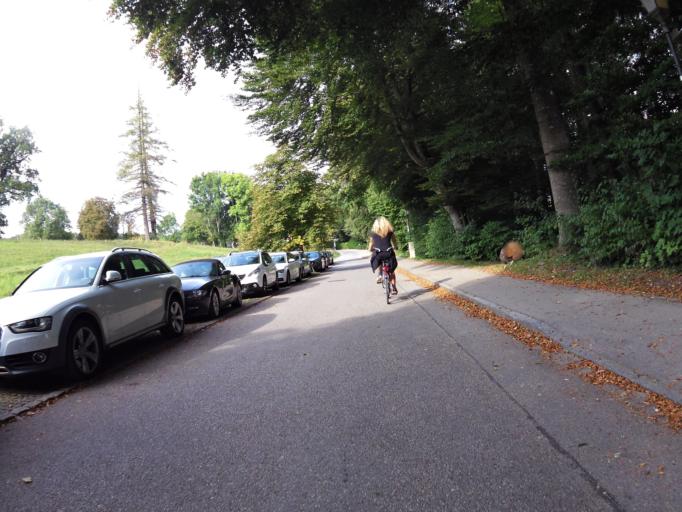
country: DE
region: Bavaria
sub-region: Upper Bavaria
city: Pocking
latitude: 47.9571
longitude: 11.3124
